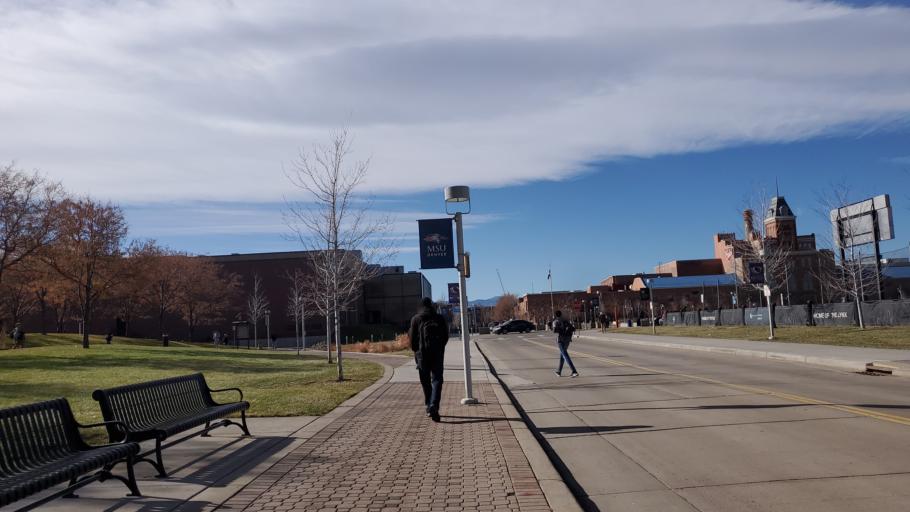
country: US
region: Colorado
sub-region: Denver County
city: Denver
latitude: 39.7458
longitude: -105.0028
